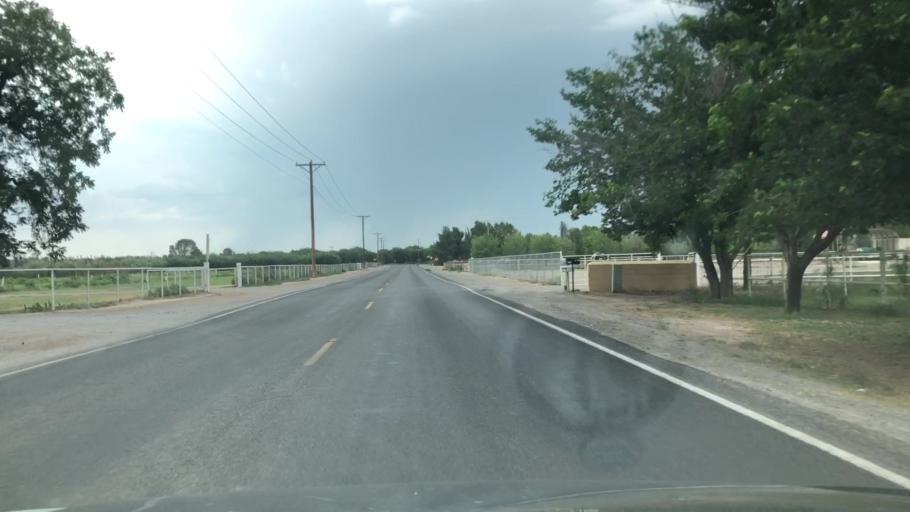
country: US
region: Texas
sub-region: El Paso County
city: Canutillo
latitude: 31.9290
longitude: -106.6289
